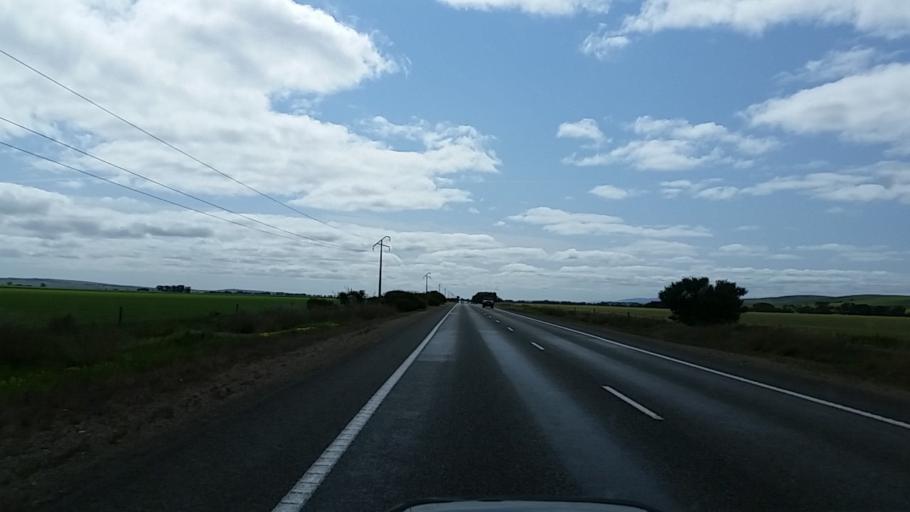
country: AU
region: South Australia
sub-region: Port Pirie City and Dists
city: Crystal Brook
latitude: -33.5107
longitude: 138.1875
